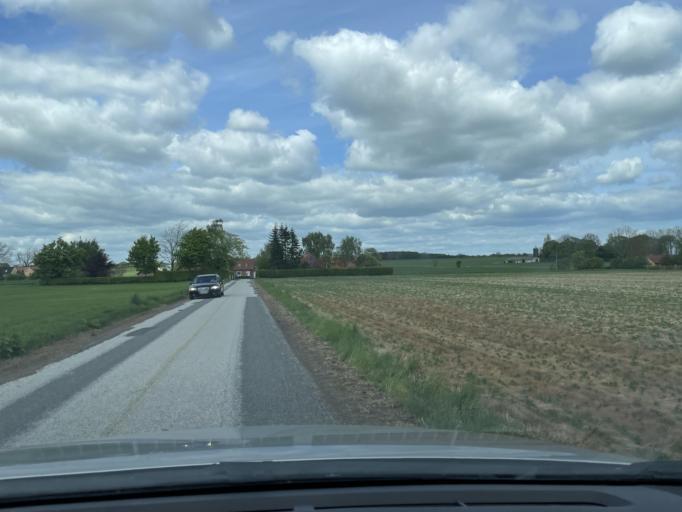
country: DK
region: Central Jutland
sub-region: Odder Kommune
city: Odder
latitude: 55.9084
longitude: 10.1202
